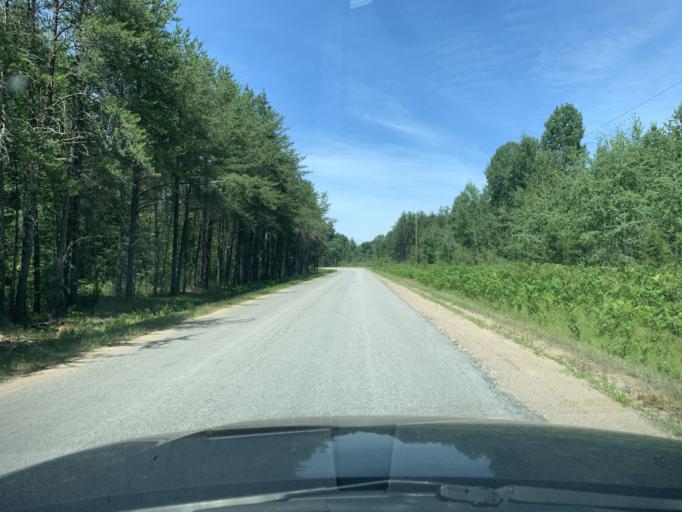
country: CA
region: Ontario
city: Petawawa
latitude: 45.6604
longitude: -77.6061
